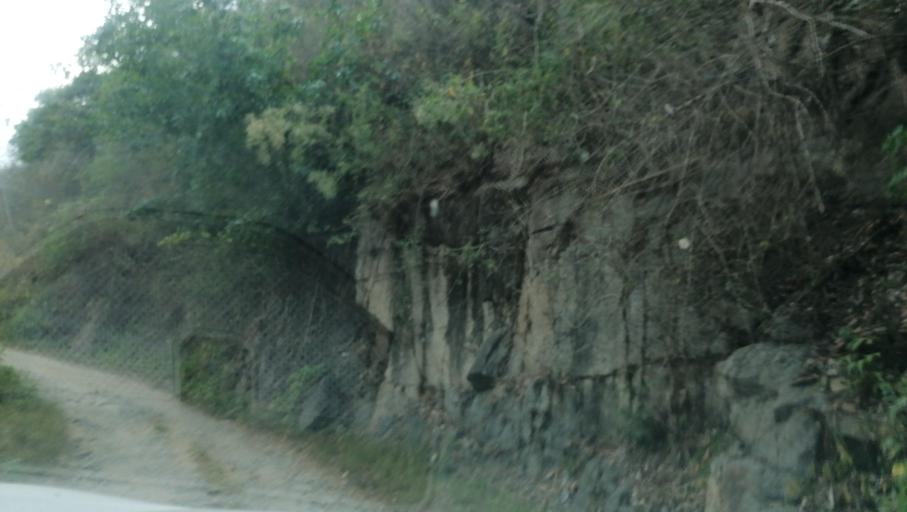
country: MX
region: Chiapas
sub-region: Cacahoatan
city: Benito Juarez
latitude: 15.1551
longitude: -92.1838
